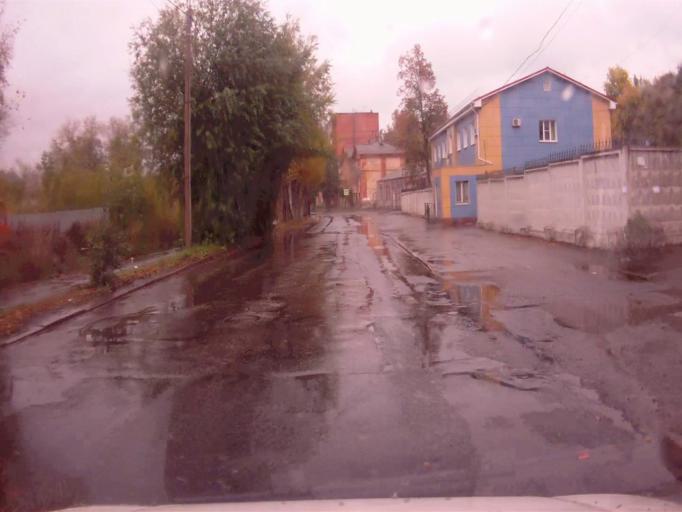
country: RU
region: Chelyabinsk
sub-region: Gorod Chelyabinsk
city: Chelyabinsk
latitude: 55.1944
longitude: 61.4108
